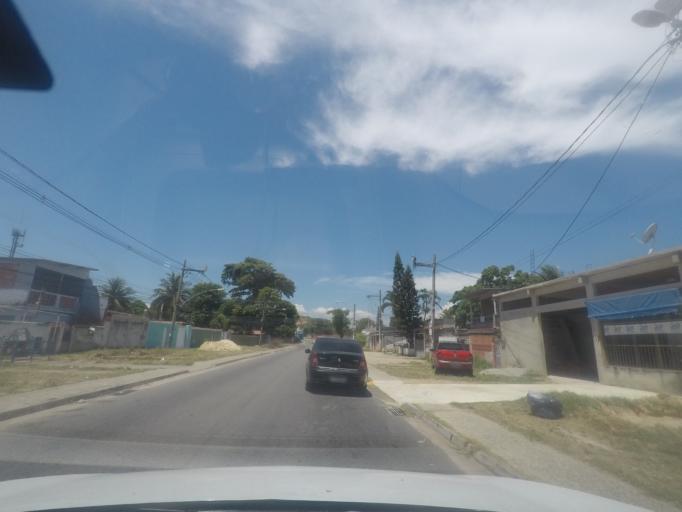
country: BR
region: Rio de Janeiro
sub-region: Itaguai
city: Itaguai
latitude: -22.9792
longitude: -43.6815
